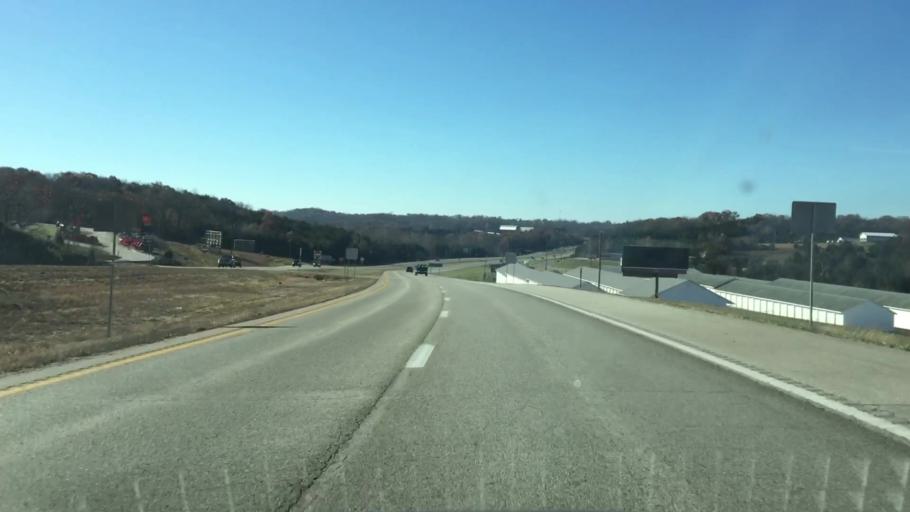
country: US
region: Missouri
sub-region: Cole County
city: Wardsville
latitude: 38.5327
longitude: -92.2190
